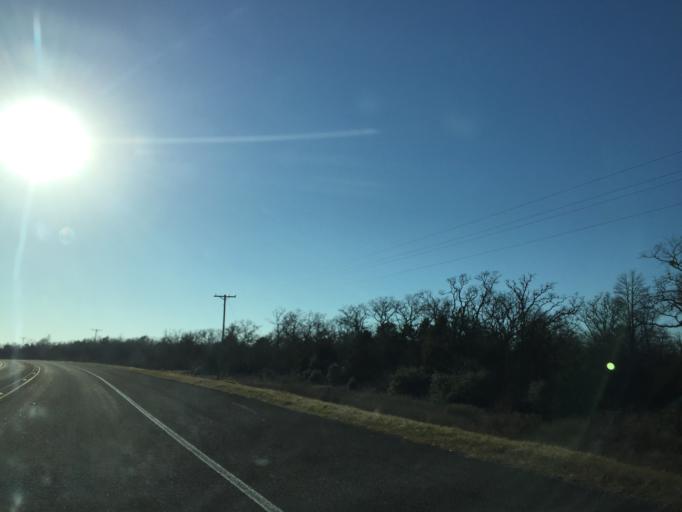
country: US
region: Texas
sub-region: Bastrop County
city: Elgin
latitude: 30.3760
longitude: -97.2564
